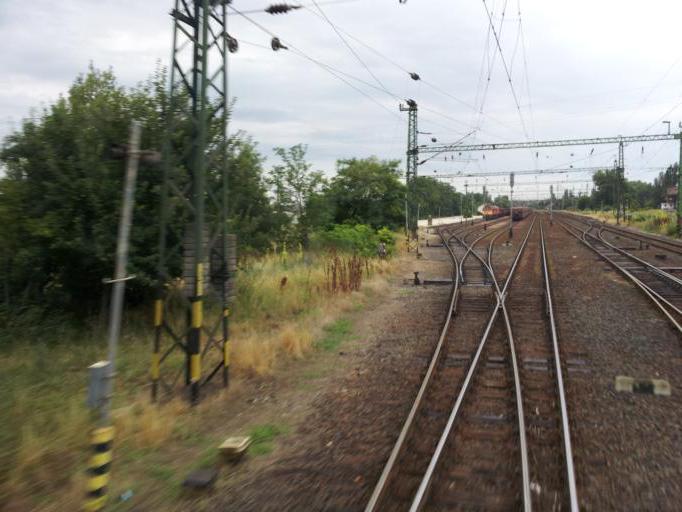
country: HU
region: Fejer
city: Szabadbattyan
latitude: 47.1081
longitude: 18.3938
